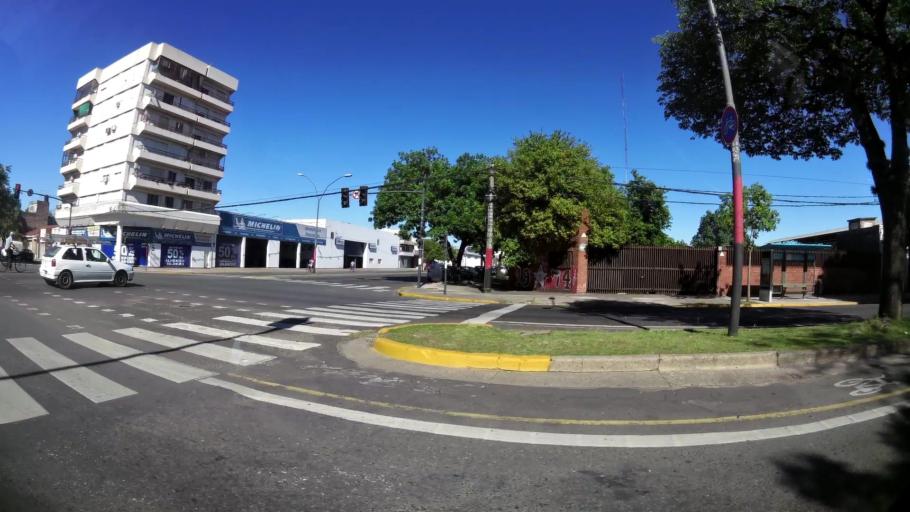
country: AR
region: Santa Fe
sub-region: Departamento de Rosario
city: Rosario
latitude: -32.9625
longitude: -60.6708
